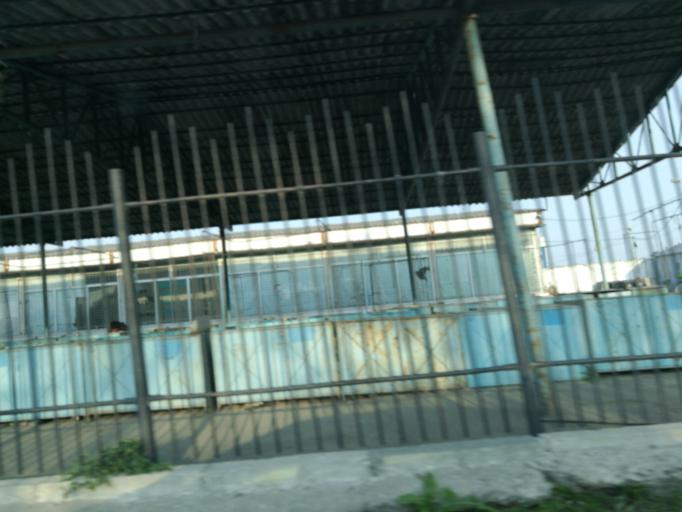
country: RO
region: Constanta
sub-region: Municipiul Constanta
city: Palazu Mare
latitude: 44.2040
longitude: 28.6109
